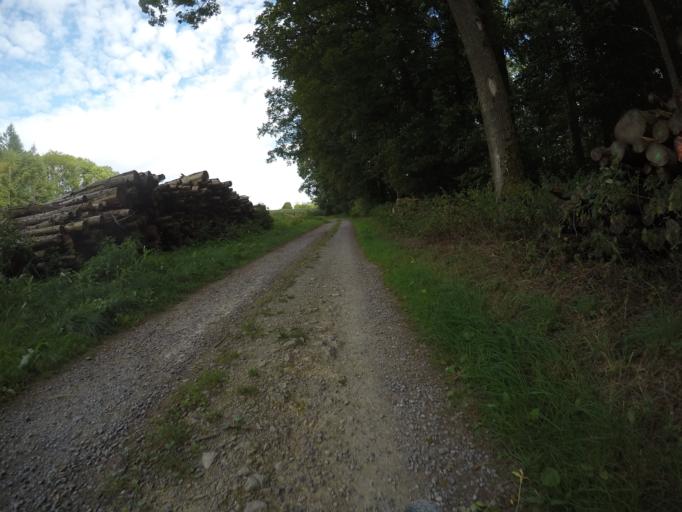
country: DE
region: Baden-Wuerttemberg
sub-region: Regierungsbezirk Stuttgart
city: Eberdingen
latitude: 48.8434
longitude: 8.9699
